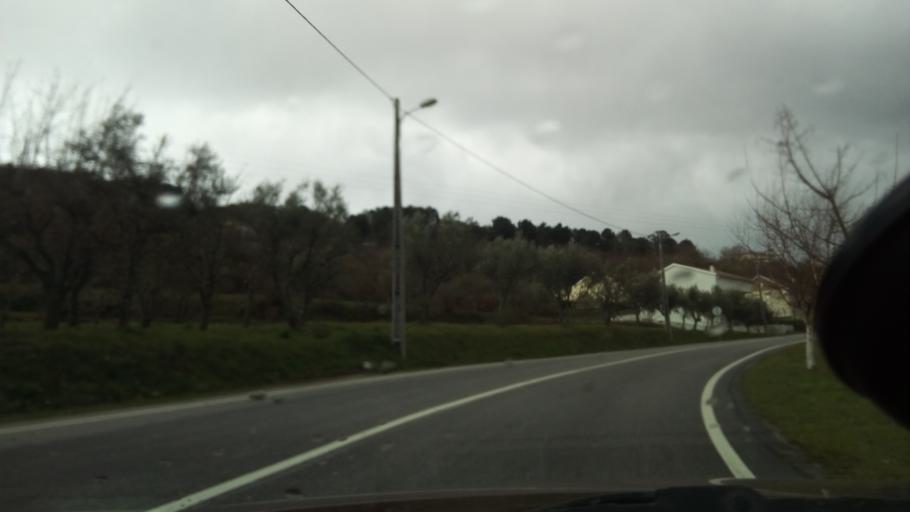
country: PT
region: Guarda
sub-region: Manteigas
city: Manteigas
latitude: 40.5036
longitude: -7.5837
